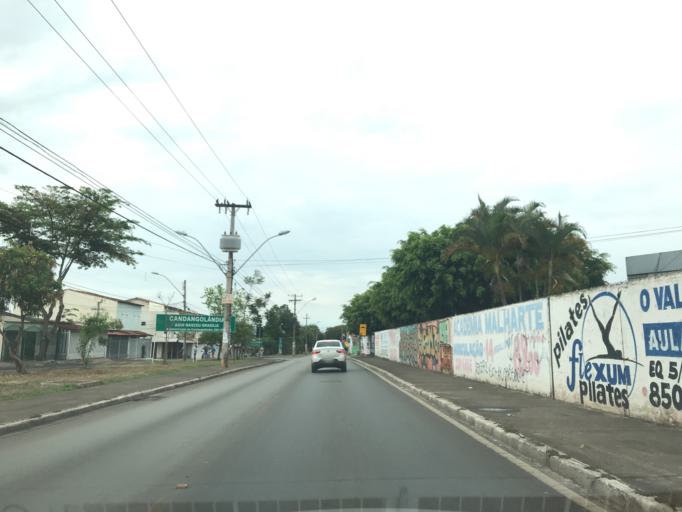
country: BR
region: Federal District
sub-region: Brasilia
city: Brasilia
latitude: -15.8509
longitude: -47.9539
